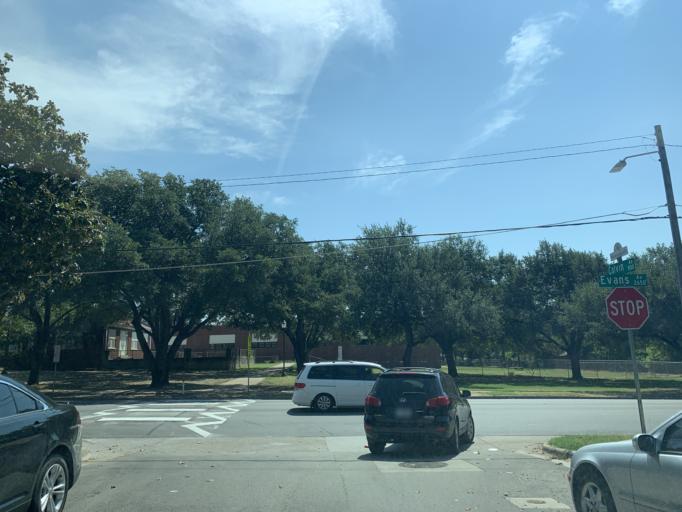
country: US
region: Texas
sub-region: Tarrant County
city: Fort Worth
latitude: 32.7139
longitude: -97.3187
